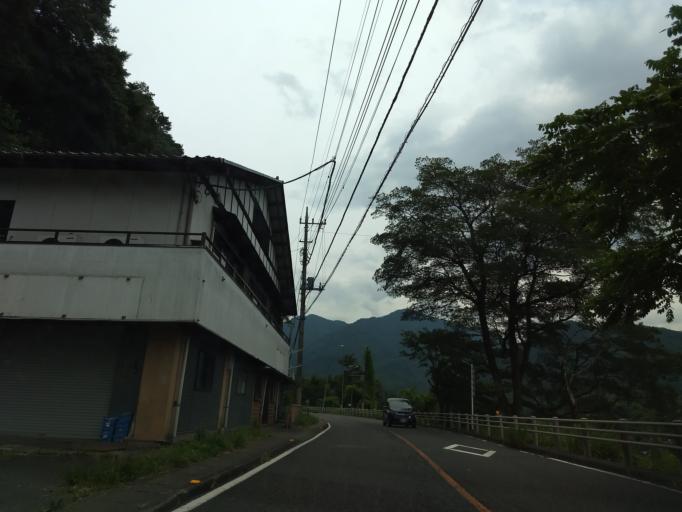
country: JP
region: Yamanashi
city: Otsuki
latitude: 35.6138
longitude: 138.9943
